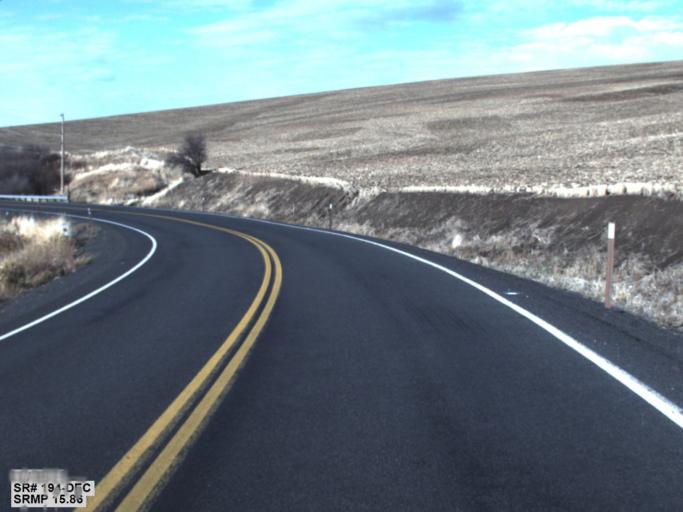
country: US
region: Washington
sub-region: Whitman County
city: Pullman
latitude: 46.7307
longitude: -117.3049
